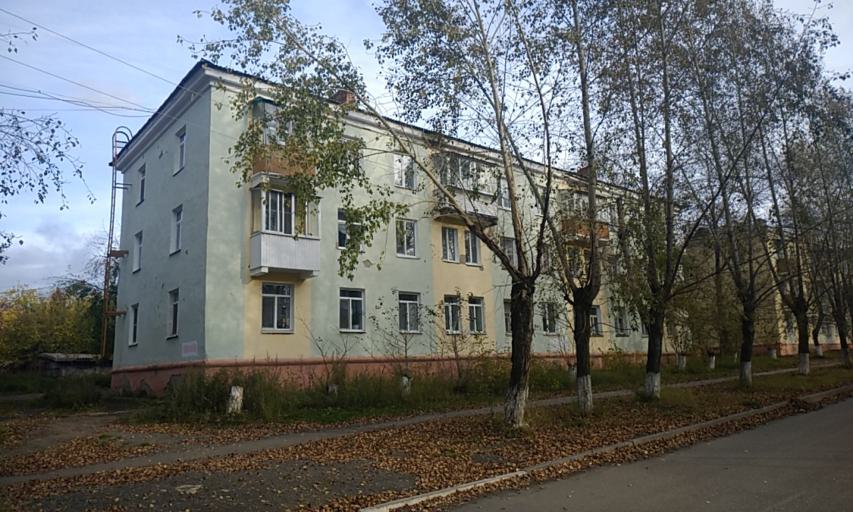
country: RU
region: Sverdlovsk
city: Krasnoural'sk
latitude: 58.3551
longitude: 60.0557
